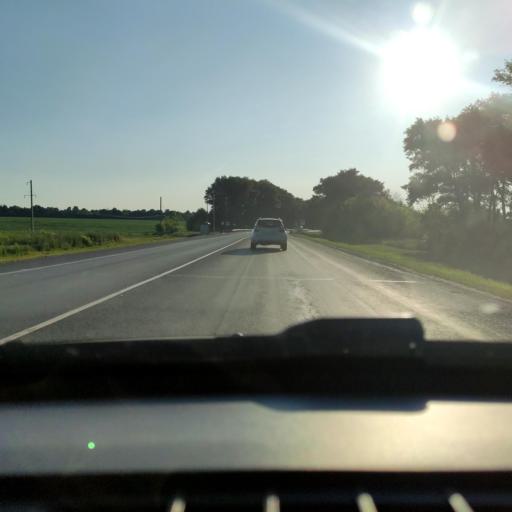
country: RU
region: Voronezj
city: Kashirskoye
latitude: 51.4905
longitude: 39.6219
